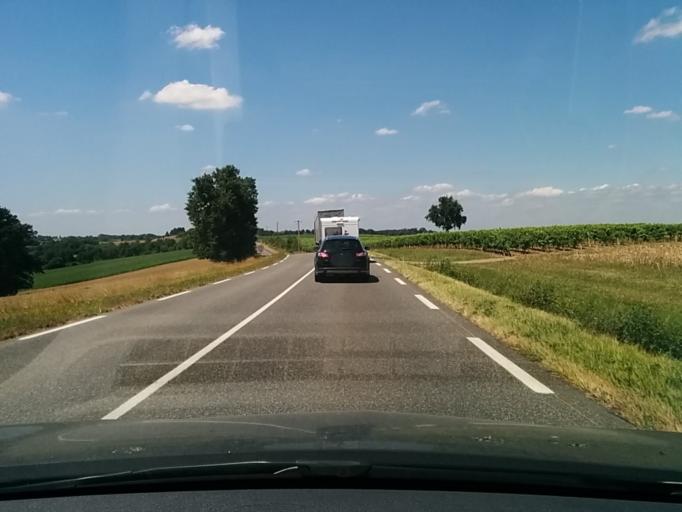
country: FR
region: Midi-Pyrenees
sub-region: Departement du Gers
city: Eauze
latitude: 43.7812
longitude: 0.1168
